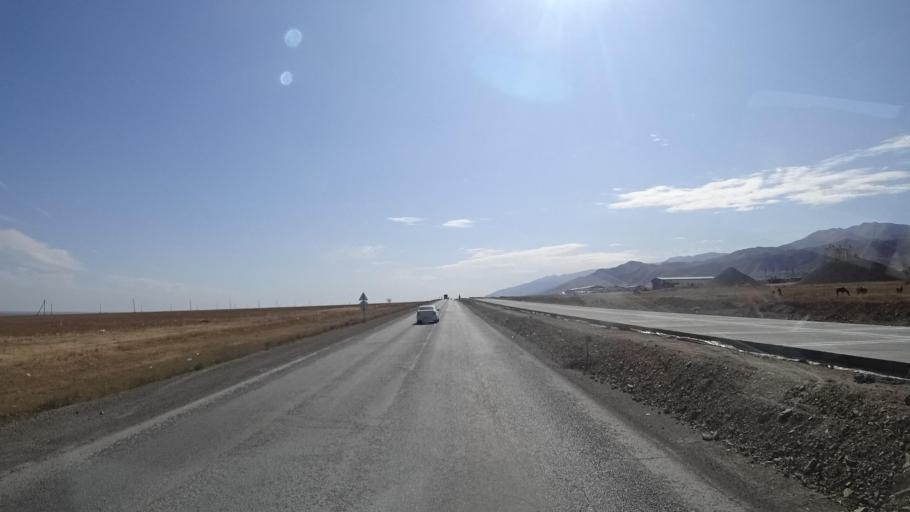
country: KG
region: Chuy
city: Ivanovka
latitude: 43.3917
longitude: 75.1386
